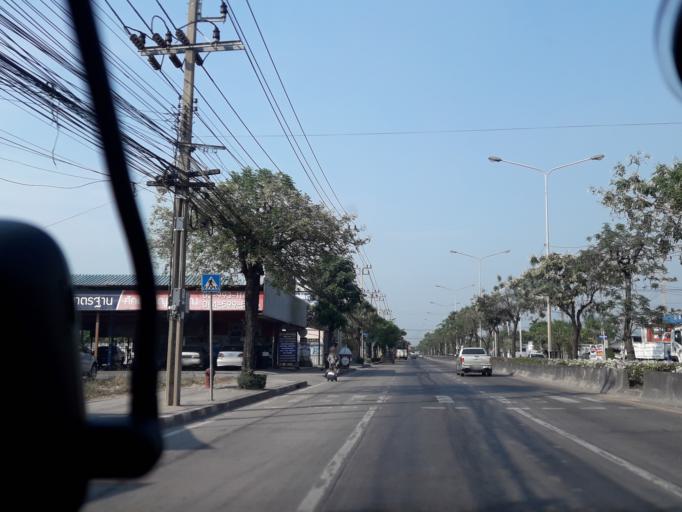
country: TH
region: Pathum Thani
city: Lam Luk Ka
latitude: 13.8859
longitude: 100.7317
